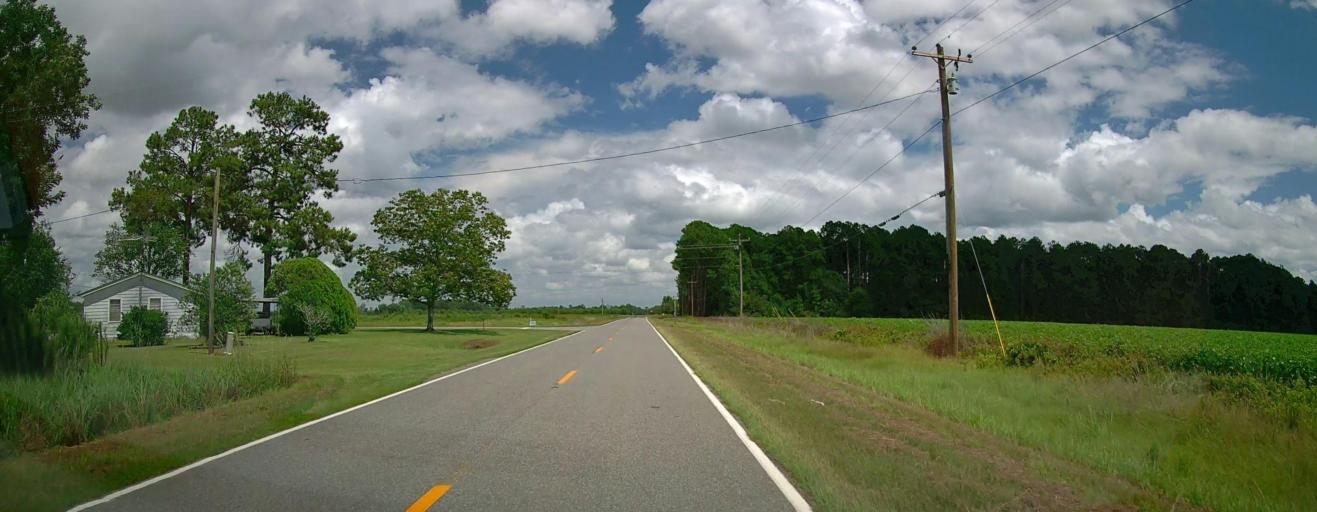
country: US
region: Georgia
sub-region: Irwin County
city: Ocilla
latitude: 31.6463
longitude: -83.2916
